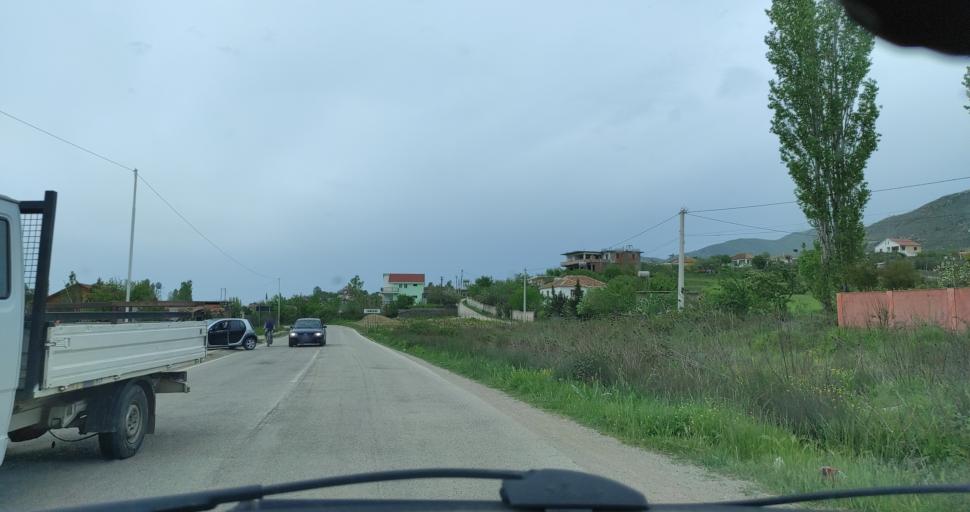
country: AL
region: Lezhe
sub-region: Rrethi i Kurbinit
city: Lac
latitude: 41.6158
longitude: 19.7120
